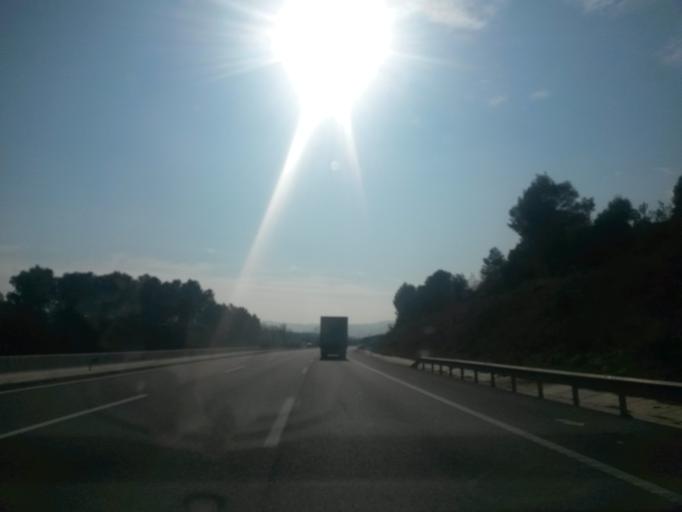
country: ES
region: Catalonia
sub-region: Provincia de Girona
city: Cervia de Ter
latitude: 42.0806
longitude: 2.8897
